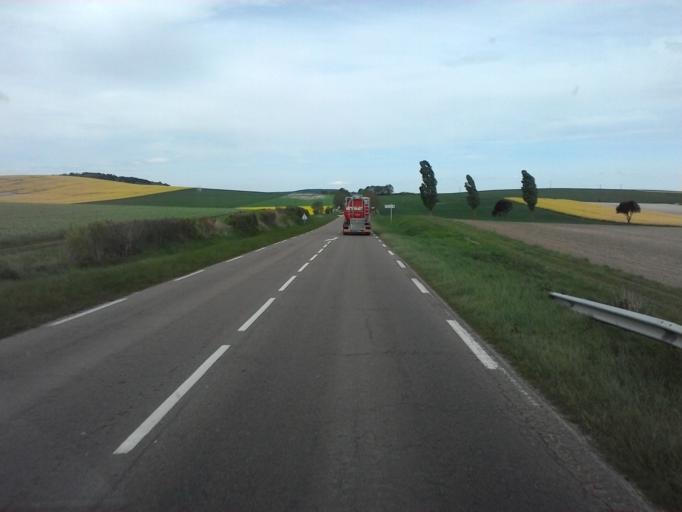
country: FR
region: Champagne-Ardenne
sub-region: Departement de l'Aube
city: Ervy-le-Chatel
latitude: 48.1127
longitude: 3.9360
